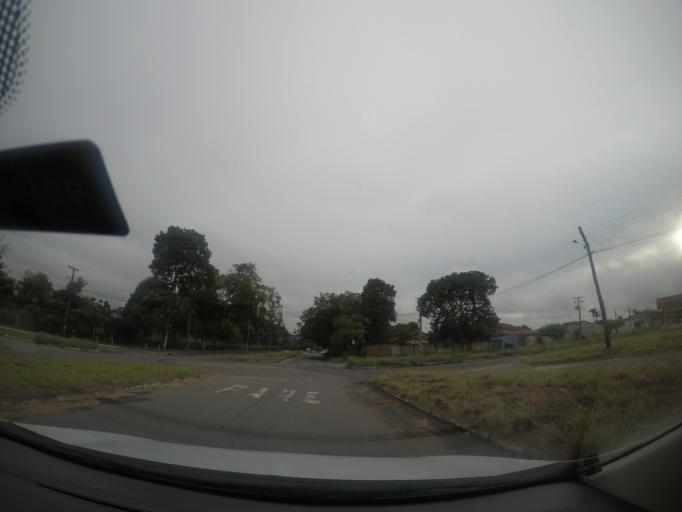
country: BR
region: Goias
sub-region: Goiania
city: Goiania
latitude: -16.7541
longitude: -49.3123
